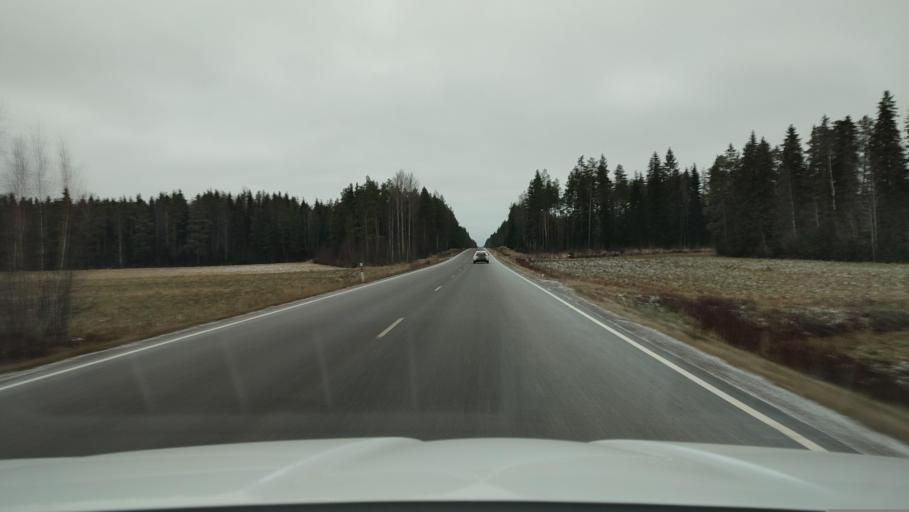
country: FI
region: Ostrobothnia
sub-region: Sydosterbotten
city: Naerpes
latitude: 62.5837
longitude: 21.4959
